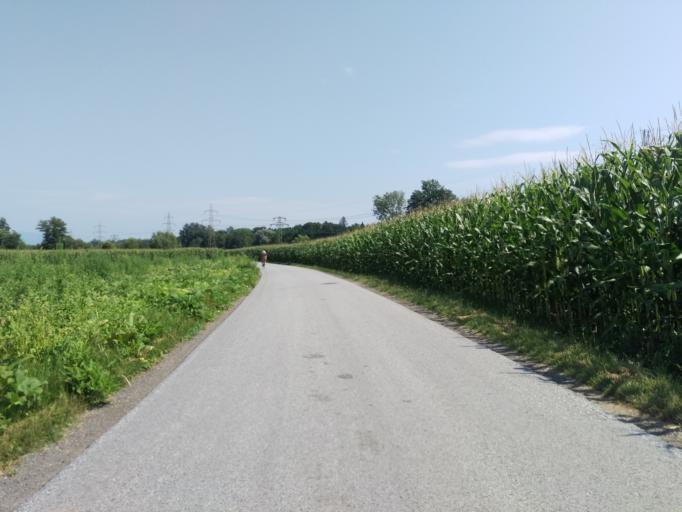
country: AT
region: Styria
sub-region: Politischer Bezirk Graz-Umgebung
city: Kalsdorf bei Graz
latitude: 46.9496
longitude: 15.4900
